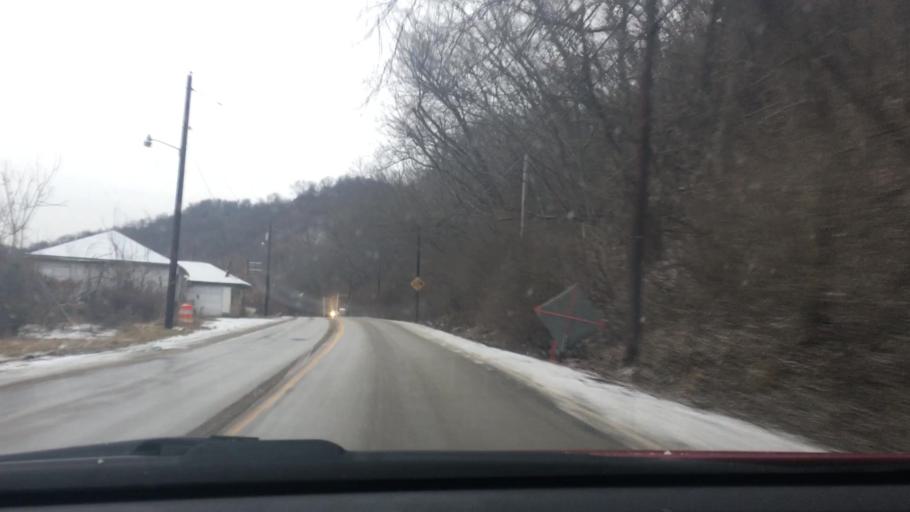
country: US
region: Pennsylvania
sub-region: Washington County
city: New Eagle
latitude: 40.2419
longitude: -79.9582
